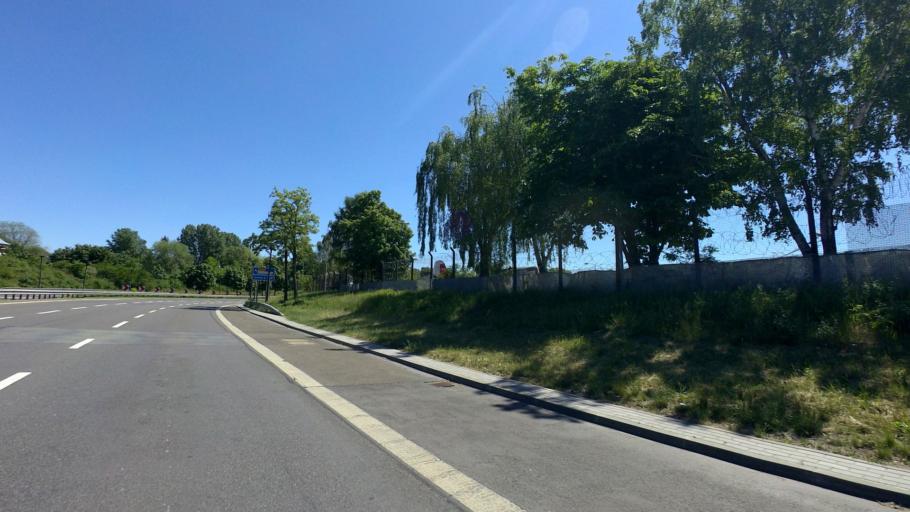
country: DE
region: Berlin
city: Reinickendorf
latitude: 52.5624
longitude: 13.3204
